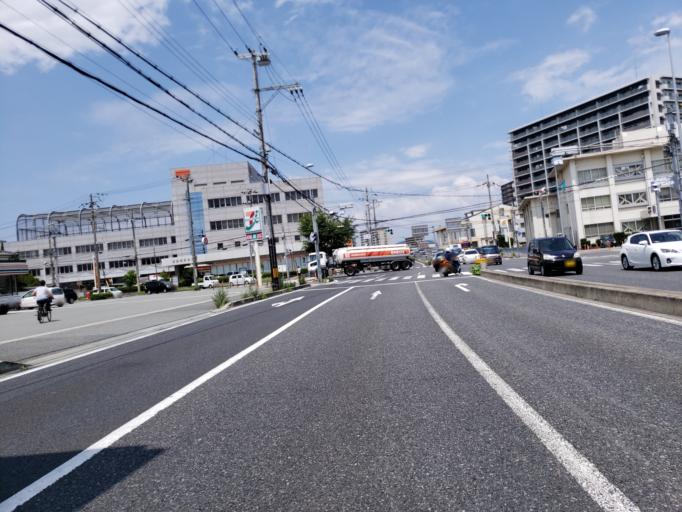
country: JP
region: Hyogo
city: Himeji
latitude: 34.7949
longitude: 134.6759
